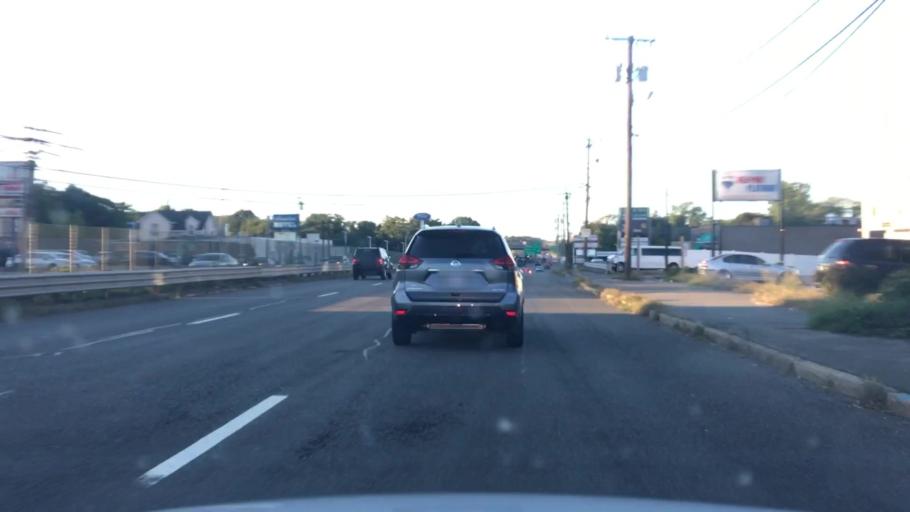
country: US
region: Massachusetts
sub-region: Essex County
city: Saugus
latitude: 42.4540
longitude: -71.0233
